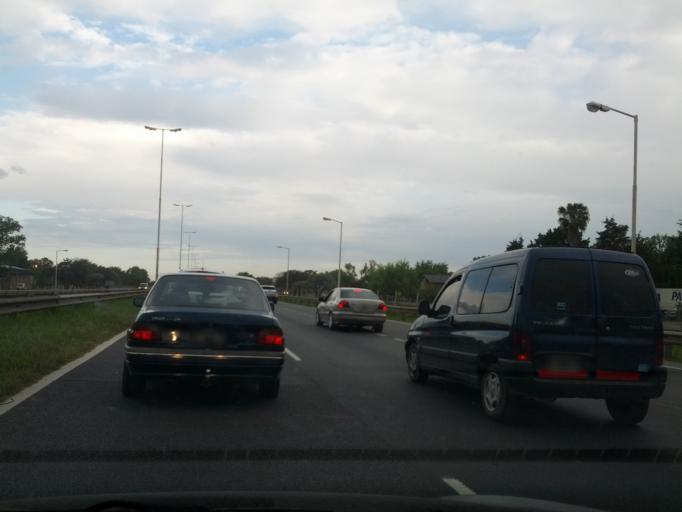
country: AR
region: Buenos Aires
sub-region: Partido de General Rodriguez
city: General Rodriguez
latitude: -34.5966
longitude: -58.9343
